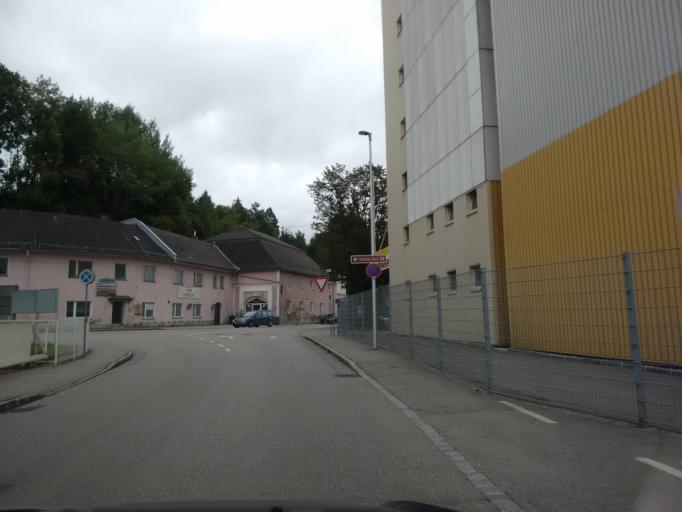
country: AT
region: Upper Austria
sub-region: Politischer Bezirk Grieskirchen
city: Grieskirchen
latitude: 48.2364
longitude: 13.8236
